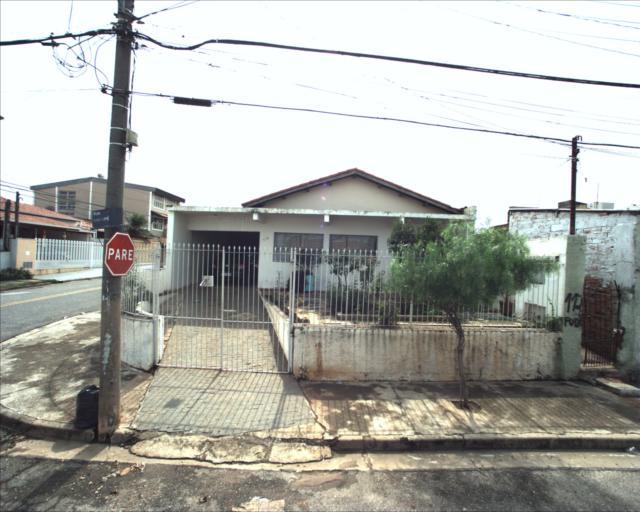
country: BR
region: Sao Paulo
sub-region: Sorocaba
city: Sorocaba
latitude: -23.5080
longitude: -47.4926
